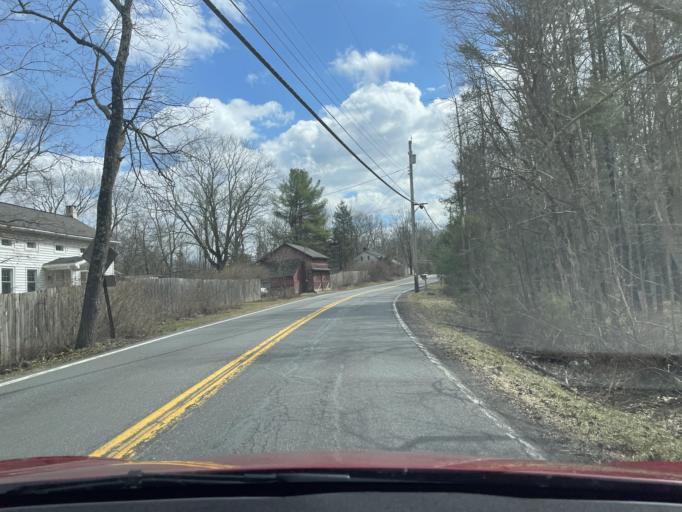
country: US
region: New York
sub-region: Ulster County
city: Zena
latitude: 42.0471
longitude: -74.0291
